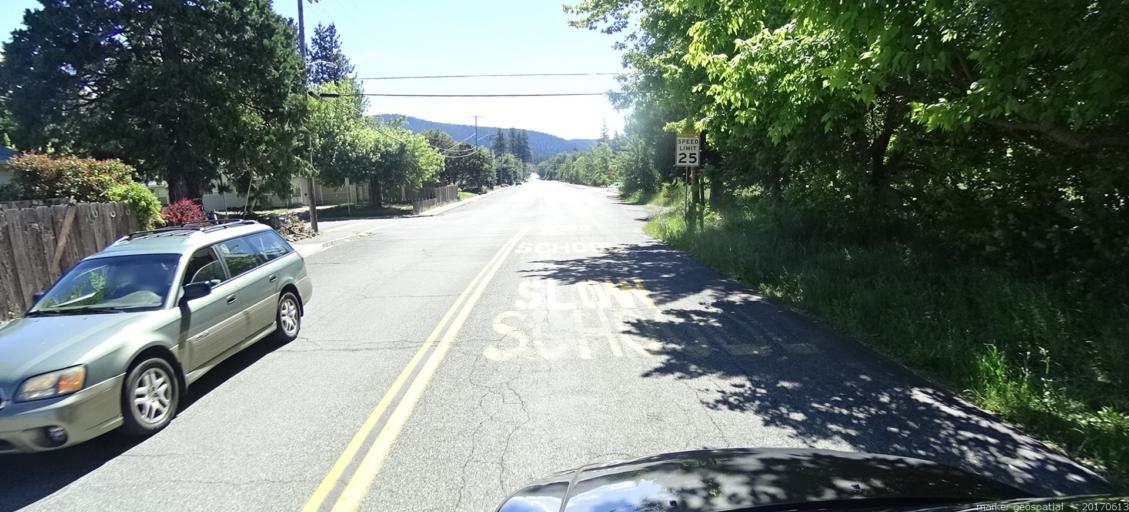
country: US
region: California
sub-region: Siskiyou County
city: Mount Shasta
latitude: 41.3197
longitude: -122.3110
